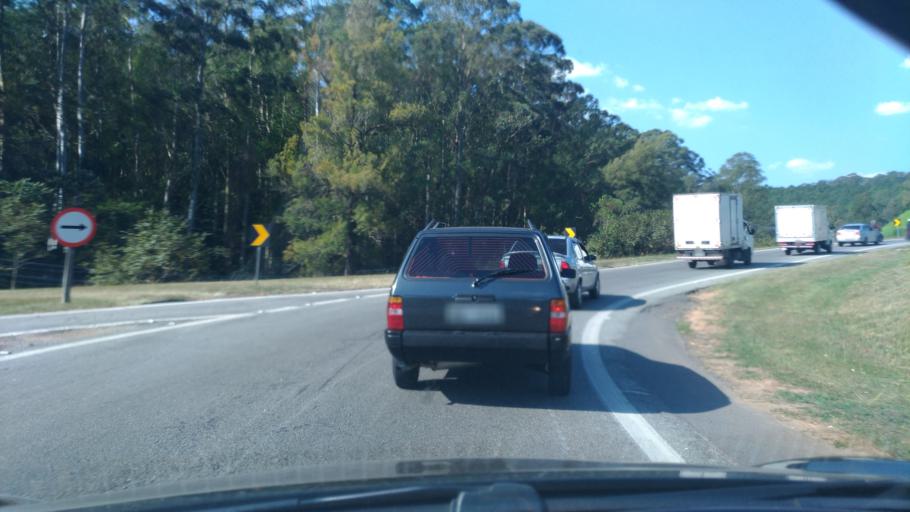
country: BR
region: Sao Paulo
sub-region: Caieiras
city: Caieiras
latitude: -23.4223
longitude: -46.7901
